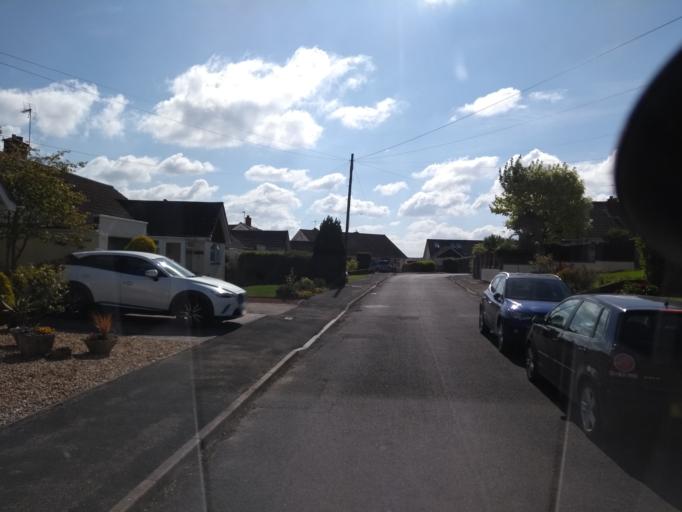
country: GB
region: England
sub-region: Somerset
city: Creech Saint Michael
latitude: 51.0286
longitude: -3.0378
